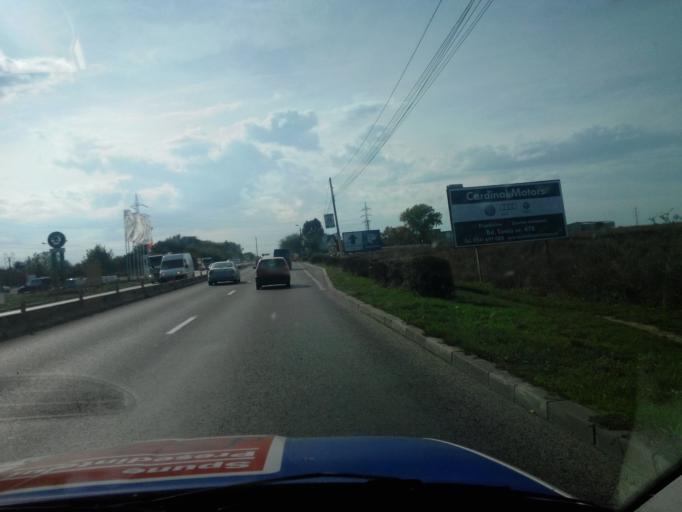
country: RO
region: Constanta
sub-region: Comuna Agigea
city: Agigea
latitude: 44.1333
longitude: 28.6184
